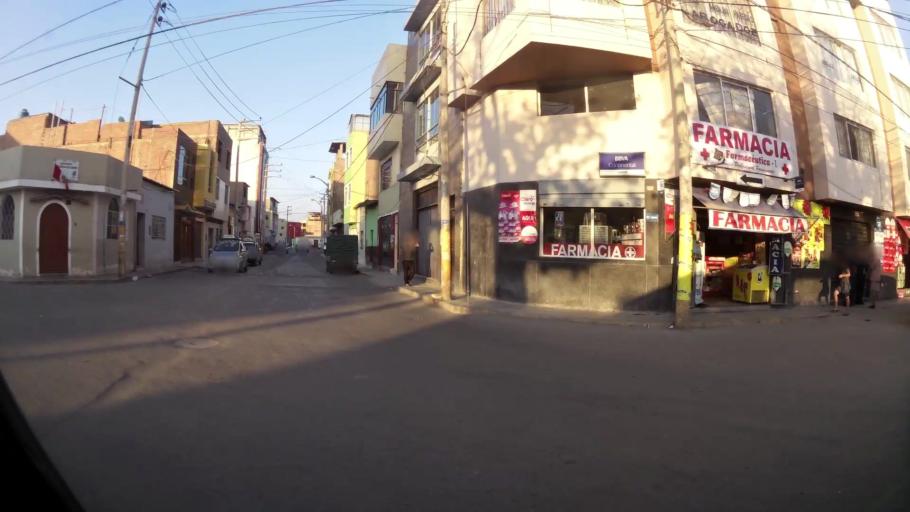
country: PE
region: Lambayeque
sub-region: Provincia de Chiclayo
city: Santa Rosa
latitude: -6.7715
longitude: -79.8342
